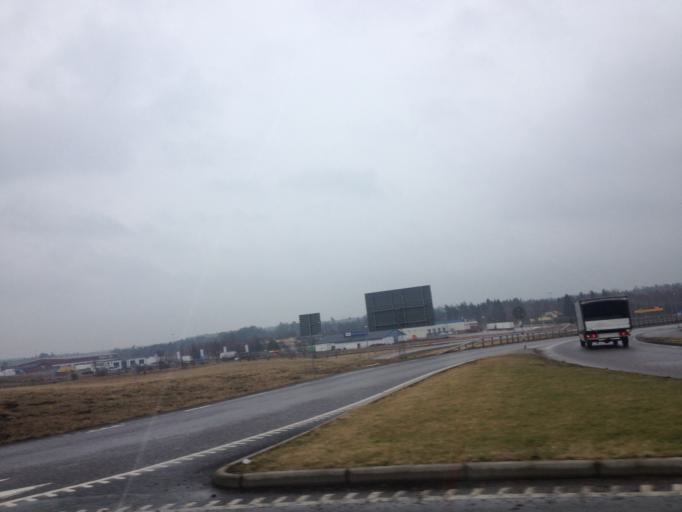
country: SE
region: Kronoberg
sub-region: Markaryds Kommun
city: Markaryd
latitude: 56.4482
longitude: 13.5992
